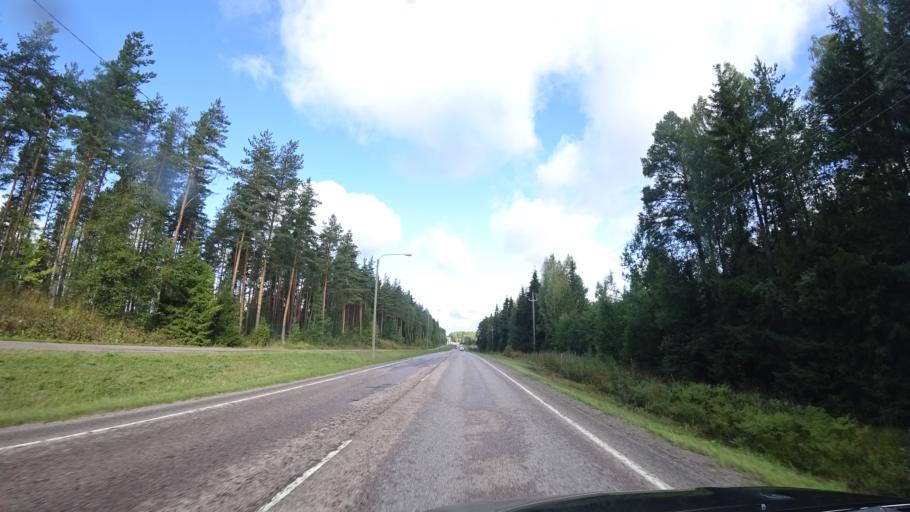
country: FI
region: Uusimaa
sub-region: Helsinki
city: Tuusula
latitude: 60.4295
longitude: 24.9935
